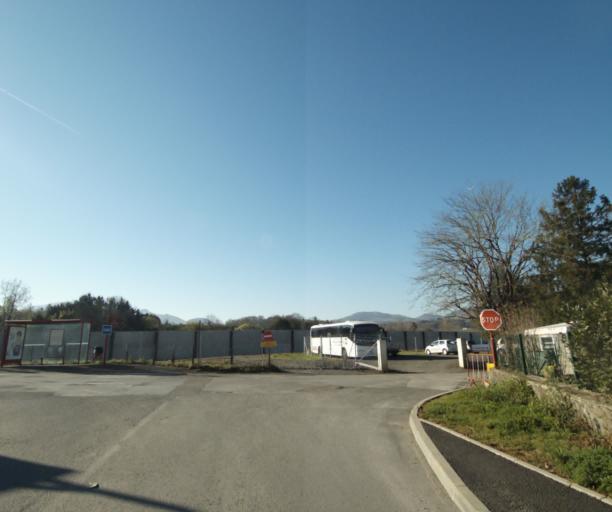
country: FR
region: Aquitaine
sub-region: Departement des Pyrenees-Atlantiques
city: Ciboure
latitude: 43.3737
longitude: -1.6735
